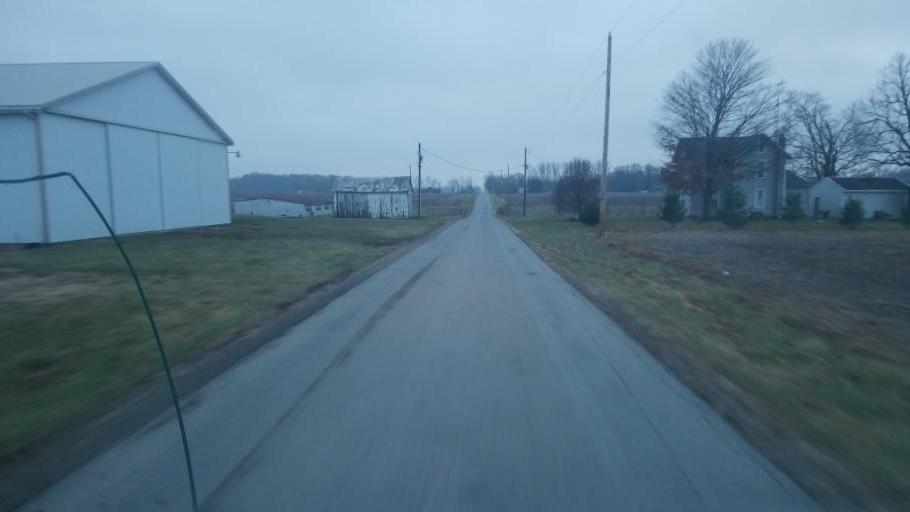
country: US
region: Ohio
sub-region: Seneca County
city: Tiffin
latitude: 40.9693
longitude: -83.1318
